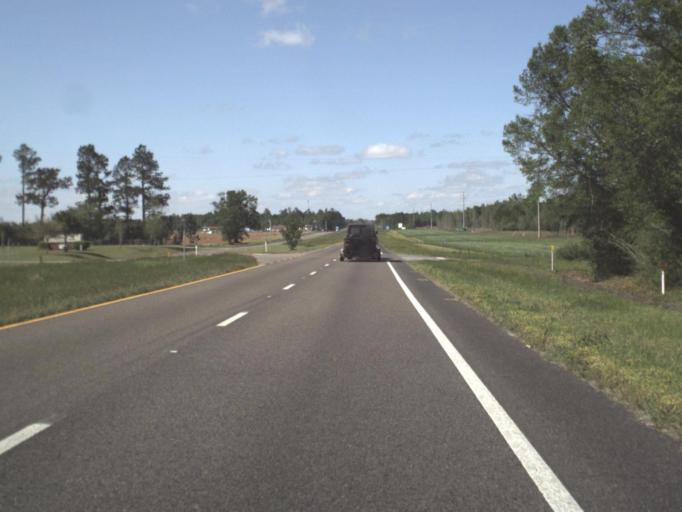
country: US
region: Florida
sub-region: Escambia County
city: Molino
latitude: 30.7236
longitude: -87.3494
